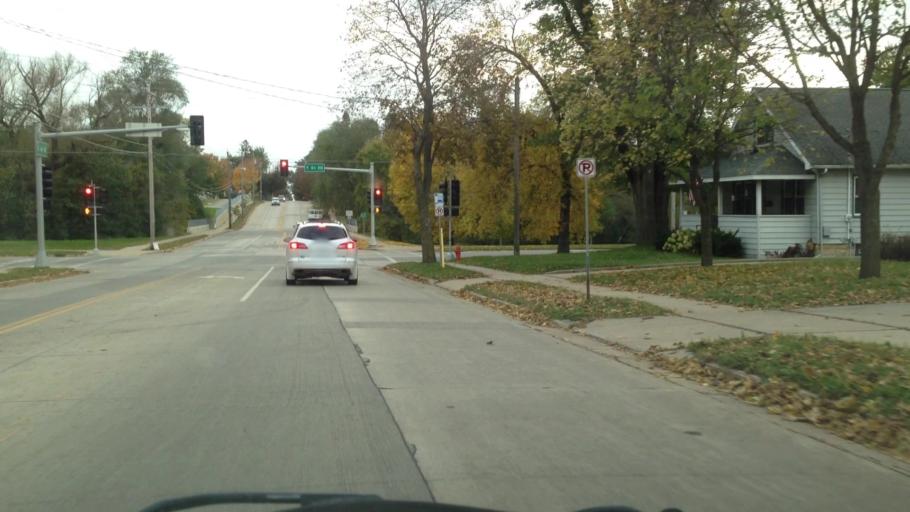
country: US
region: Minnesota
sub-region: Olmsted County
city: Rochester
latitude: 44.0305
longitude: -92.4489
